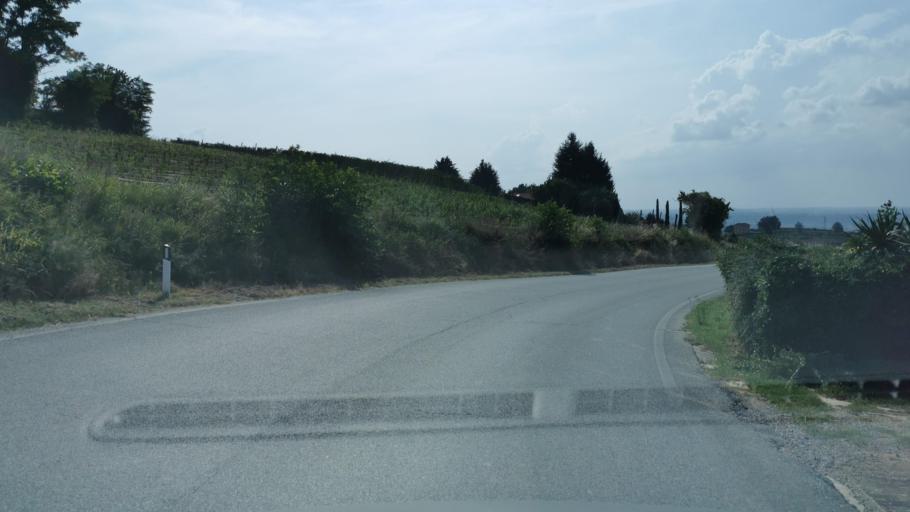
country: IT
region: Piedmont
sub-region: Provincia di Cuneo
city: La Morra
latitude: 44.6440
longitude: 7.9113
